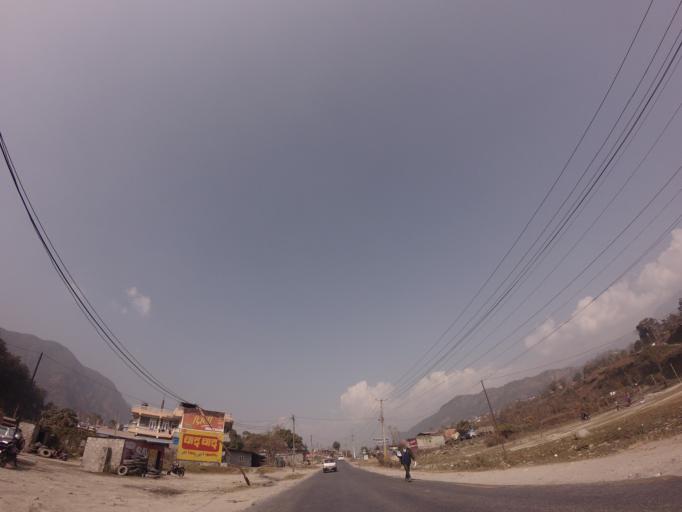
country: NP
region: Western Region
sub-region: Gandaki Zone
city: Pokhara
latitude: 28.2548
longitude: 83.9660
